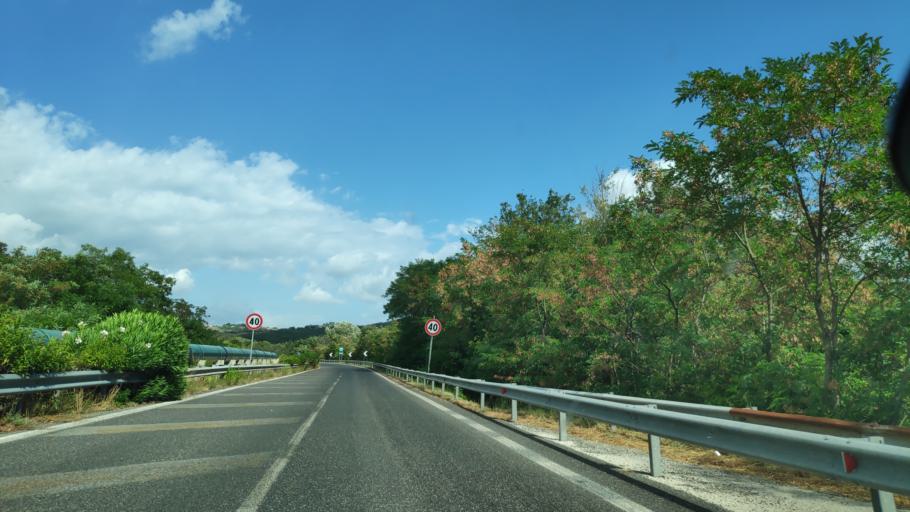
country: IT
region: Campania
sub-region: Provincia di Salerno
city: Serre
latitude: 40.6158
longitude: 15.1746
